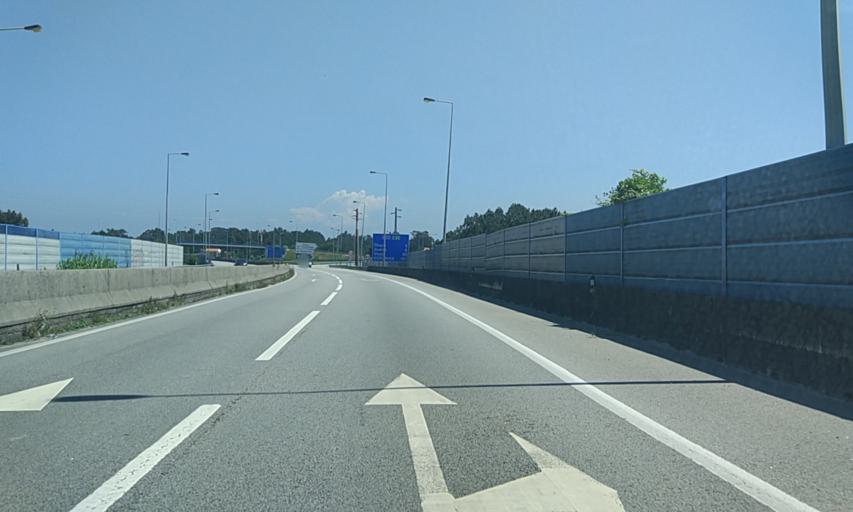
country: PT
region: Aveiro
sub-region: Ilhavo
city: Gafanha da Encarnacao
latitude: 40.6263
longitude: -8.7280
